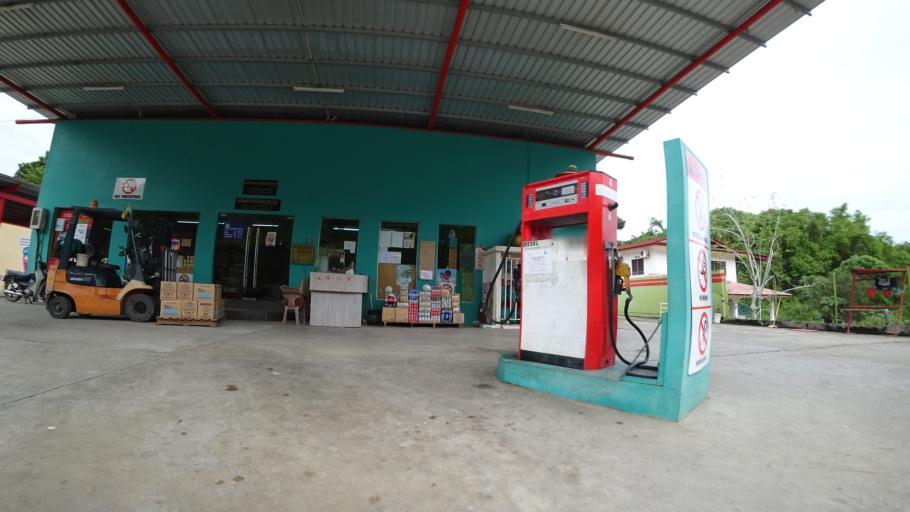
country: MY
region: Sarawak
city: Limbang
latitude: 4.6690
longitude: 114.9857
